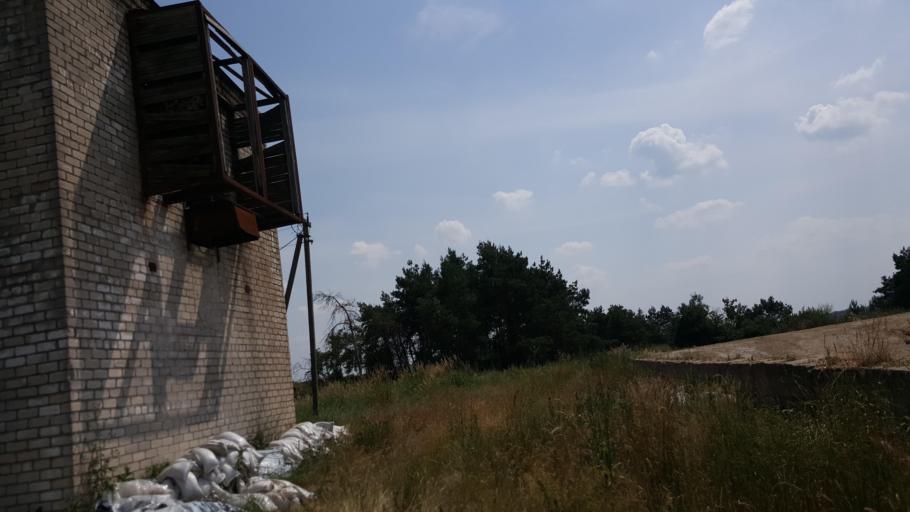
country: BY
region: Brest
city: Kamyanyets
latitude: 52.3443
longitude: 23.7681
